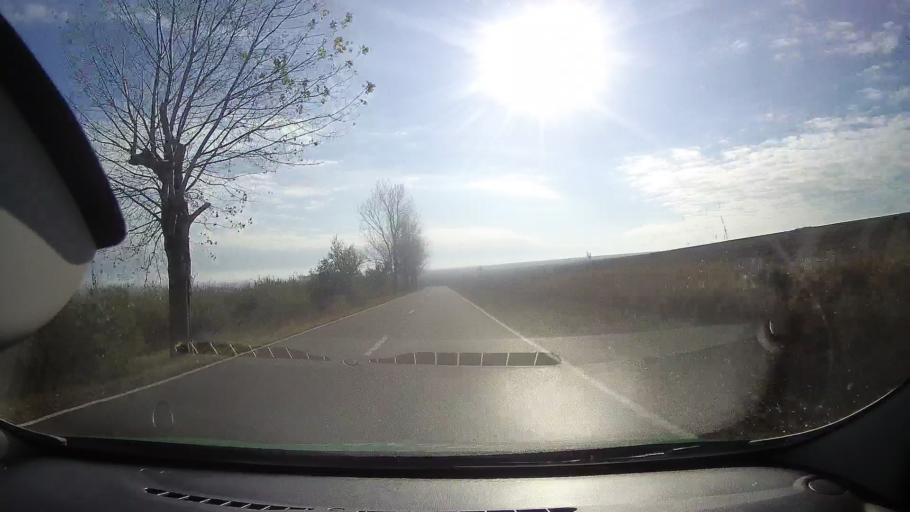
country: RO
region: Tulcea
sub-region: Comuna Mahmudia
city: Mahmudia
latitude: 45.0736
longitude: 29.0920
